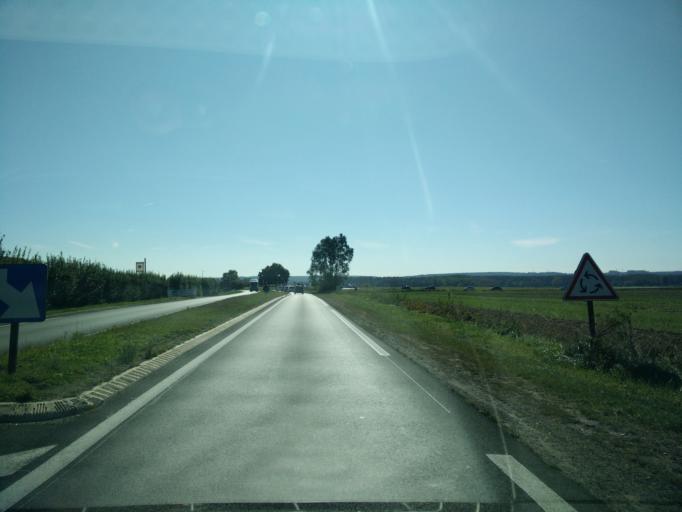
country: FR
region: Ile-de-France
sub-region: Departement de Seine-et-Marne
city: Claye-Souilly
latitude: 48.9701
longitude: 2.6619
